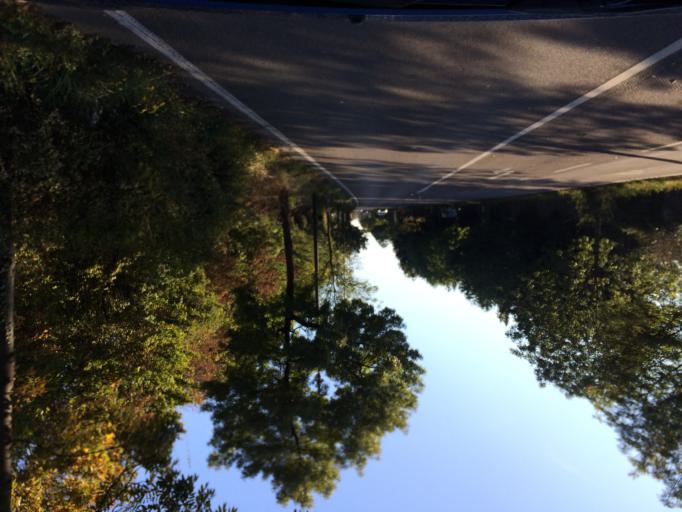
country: DE
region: North Rhine-Westphalia
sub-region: Regierungsbezirk Koln
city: Bonn
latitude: 50.7513
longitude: 7.1197
